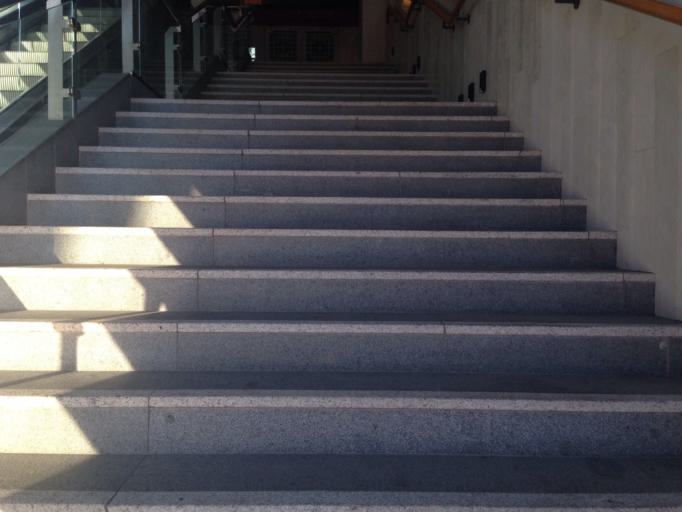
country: AU
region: New South Wales
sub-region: Willoughby
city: Chatswood
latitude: -33.7970
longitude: 151.1803
